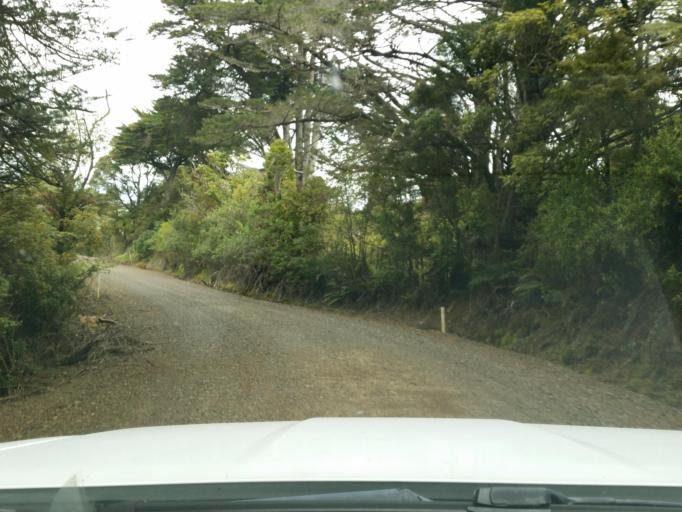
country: NZ
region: Northland
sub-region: Kaipara District
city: Dargaville
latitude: -35.7044
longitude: 173.6408
